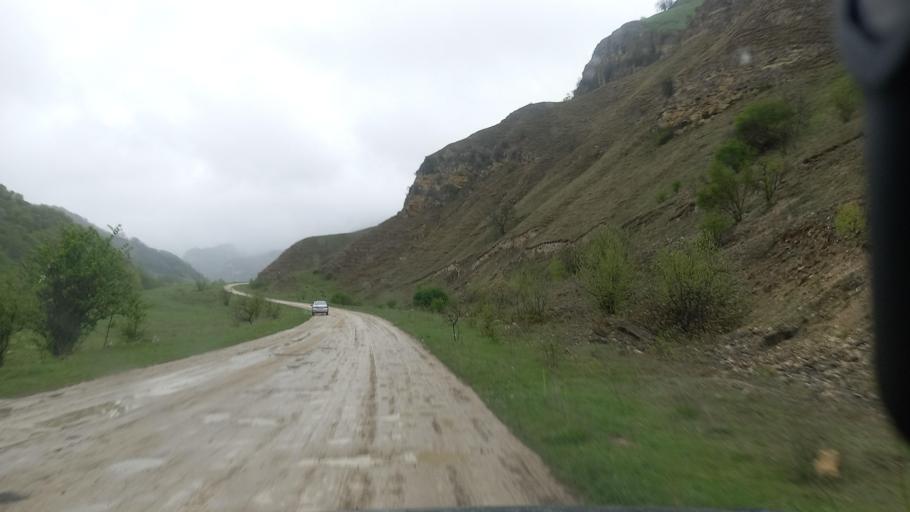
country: RU
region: Kabardino-Balkariya
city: Gundelen
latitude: 43.5968
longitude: 43.0710
